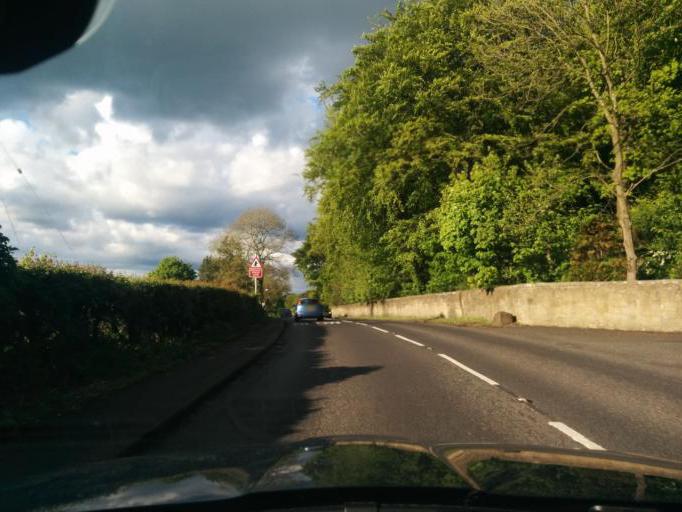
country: GB
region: England
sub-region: Northumberland
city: Bedlington
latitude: 55.1152
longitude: -1.6220
